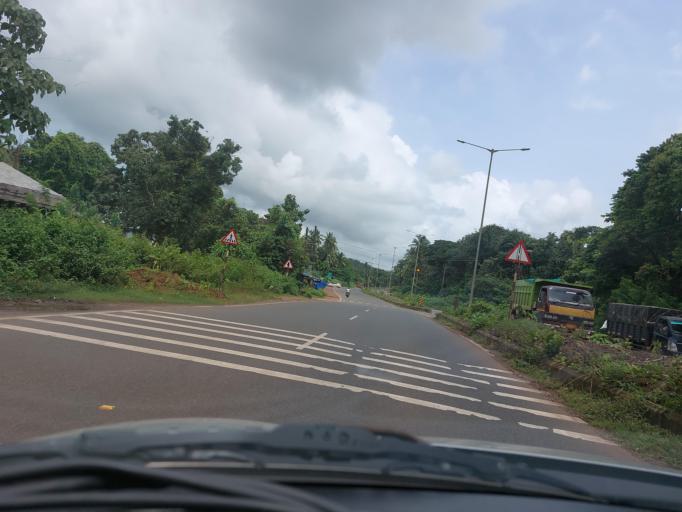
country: IN
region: Goa
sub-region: North Goa
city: Queula
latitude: 15.3877
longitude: 73.9986
